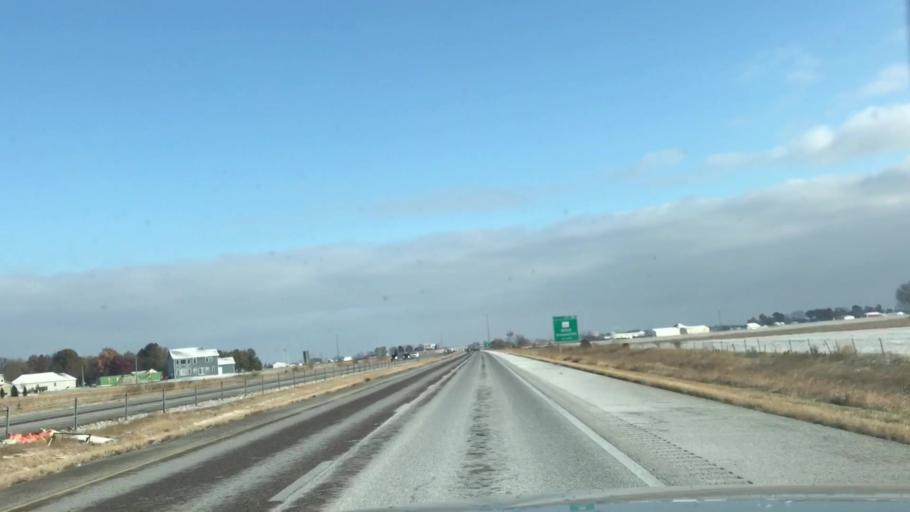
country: US
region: Illinois
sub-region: Madison County
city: Worden
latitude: 38.8796
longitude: -89.8446
